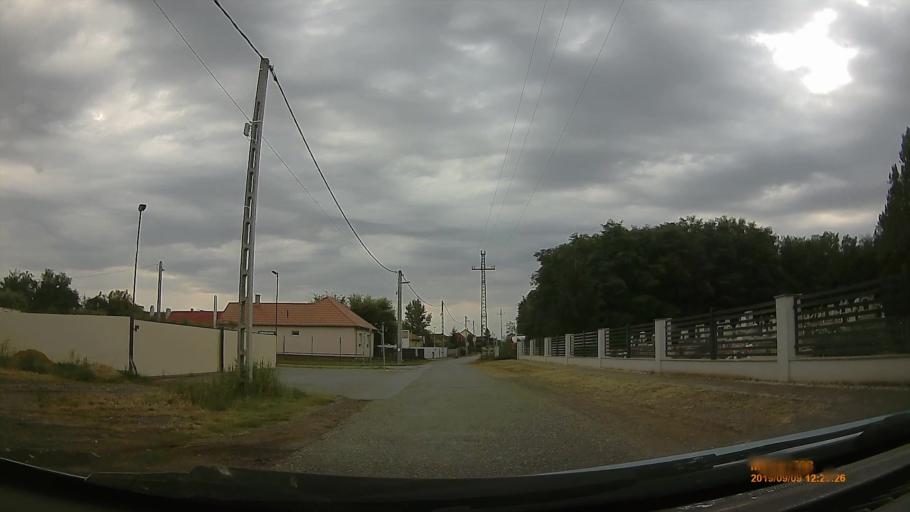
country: HU
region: Szabolcs-Szatmar-Bereg
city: Nyirpazony
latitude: 48.0110
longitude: 21.8248
